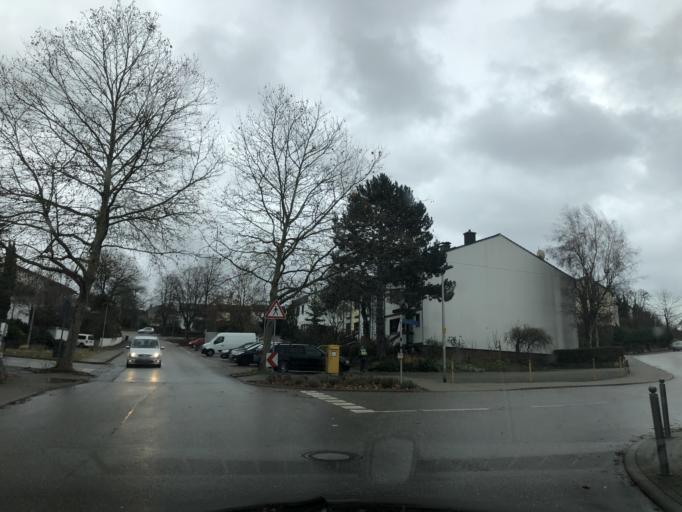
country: DE
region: Baden-Wuerttemberg
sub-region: Karlsruhe Region
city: Bammental
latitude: 49.3521
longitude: 8.7806
